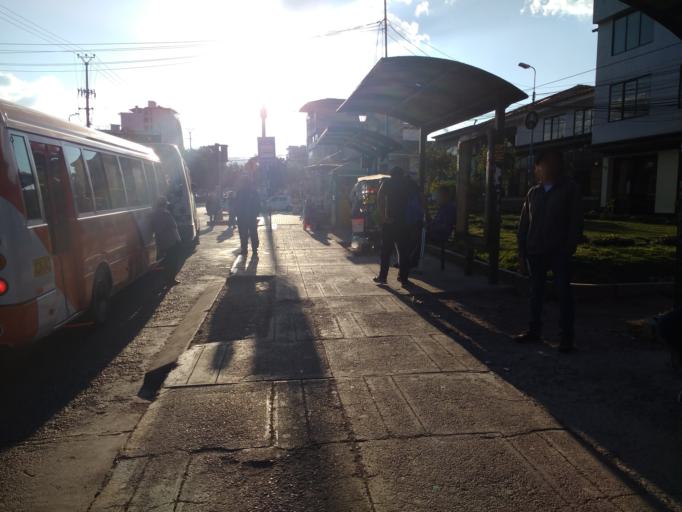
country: PE
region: Cusco
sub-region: Provincia de Cusco
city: Cusco
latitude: -13.5267
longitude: -71.9481
